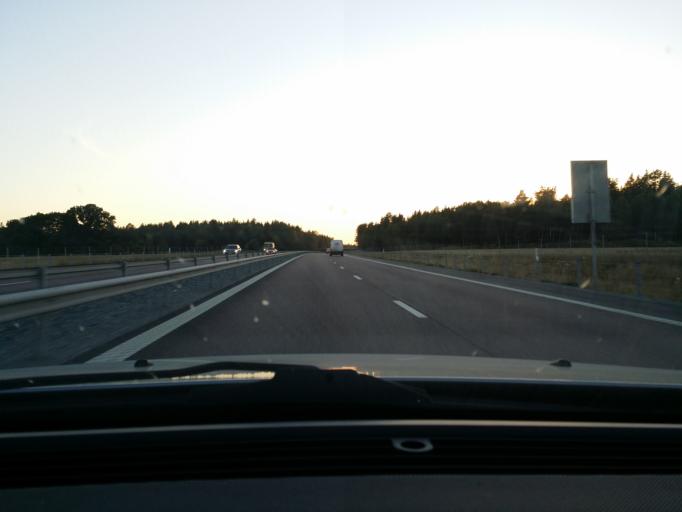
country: SE
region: Uppsala
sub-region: Enkopings Kommun
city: Hummelsta
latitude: 59.6220
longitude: 16.8012
